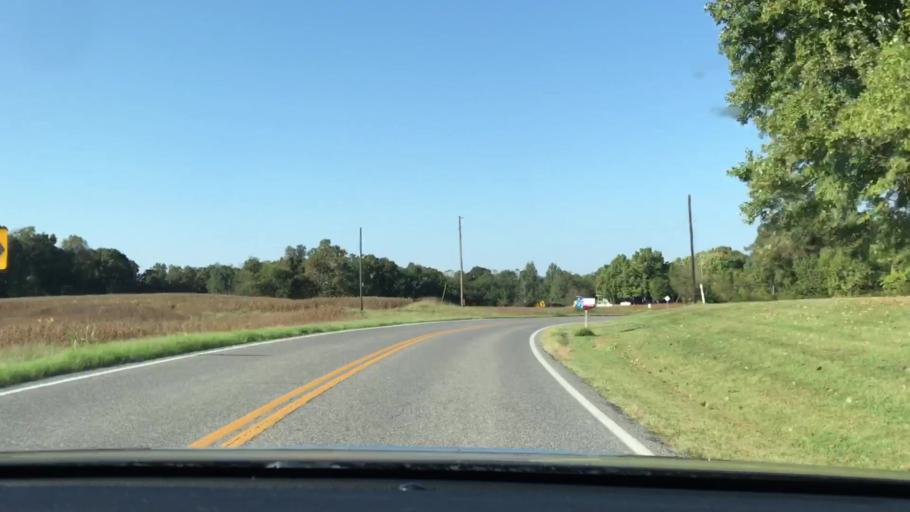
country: US
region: Kentucky
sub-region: Marshall County
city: Benton
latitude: 36.7641
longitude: -88.1954
